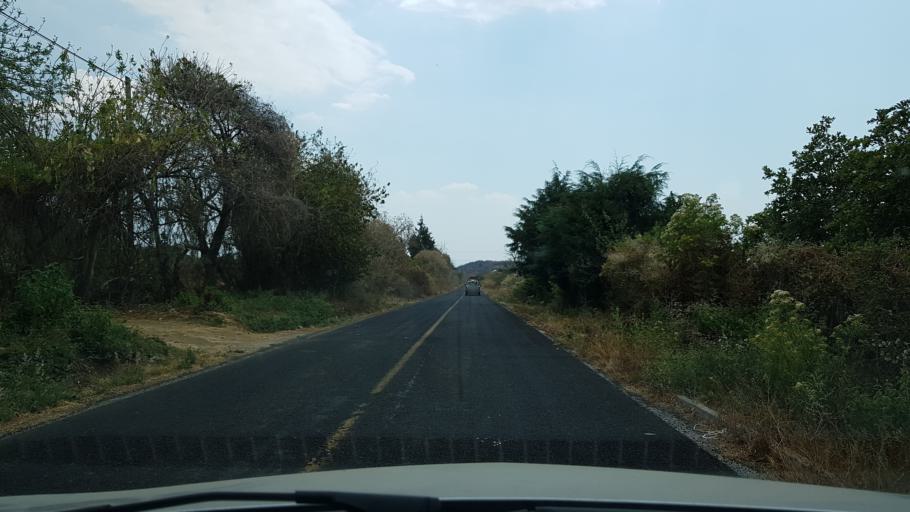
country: MX
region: Morelos
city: Tlacotepec
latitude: 18.8332
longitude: -98.7364
